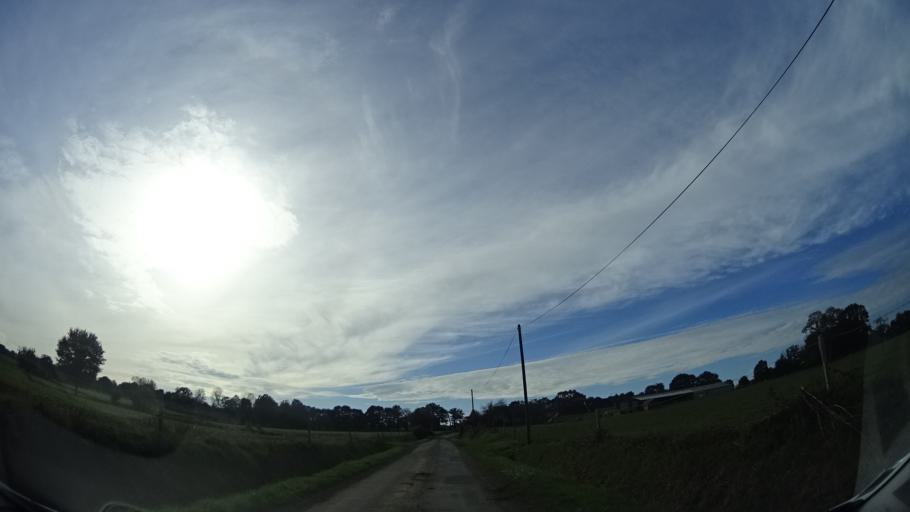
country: FR
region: Brittany
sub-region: Departement d'Ille-et-Vilaine
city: Geveze
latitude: 48.2425
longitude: -1.8229
